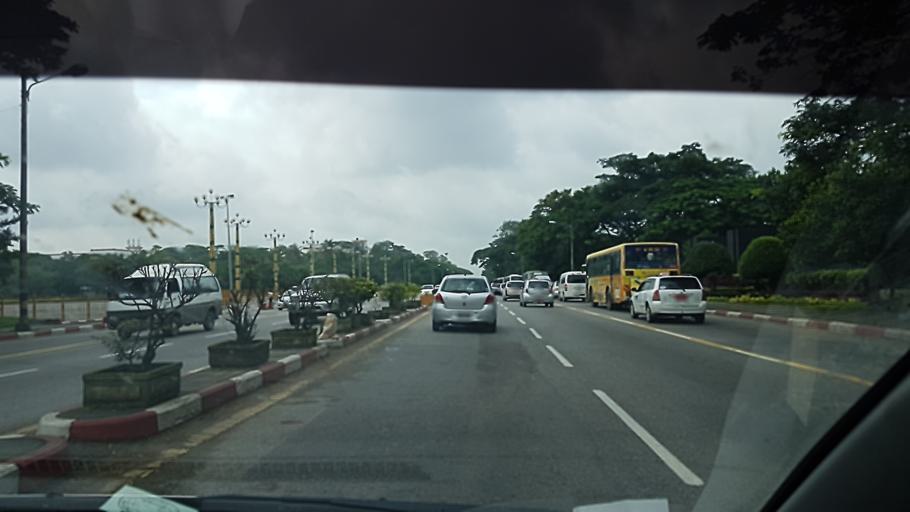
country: MM
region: Yangon
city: Yangon
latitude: 16.7969
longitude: 96.1392
